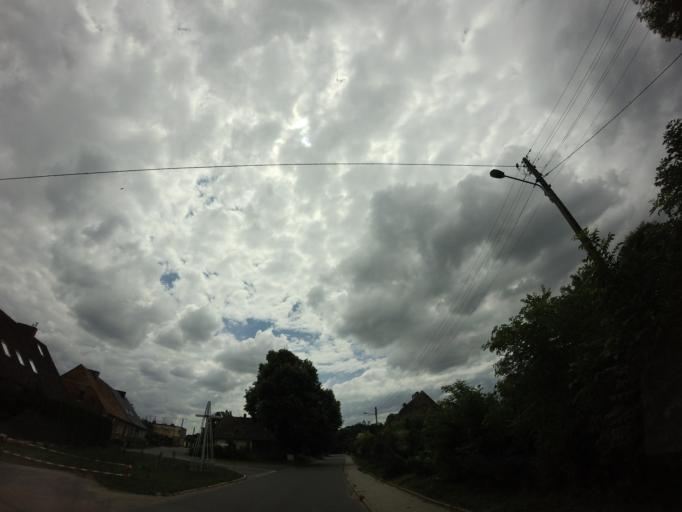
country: PL
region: West Pomeranian Voivodeship
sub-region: Powiat choszczenski
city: Choszczno
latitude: 53.1708
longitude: 15.4983
